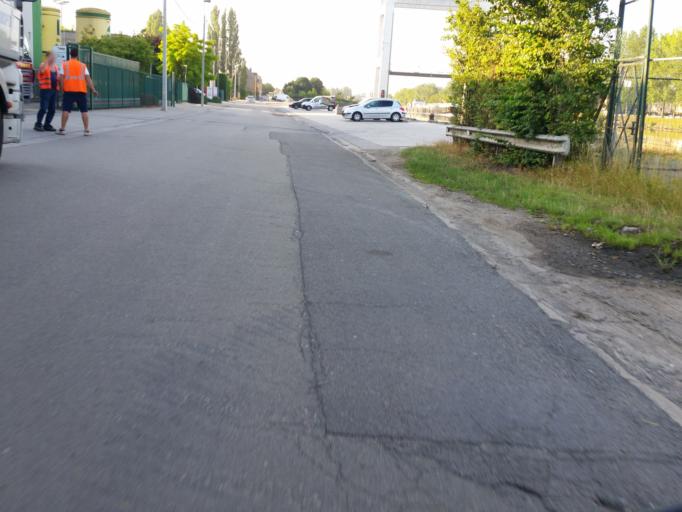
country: BE
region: Flanders
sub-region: Provincie Vlaams-Brabant
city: Vilvoorde
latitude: 50.9510
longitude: 4.4123
